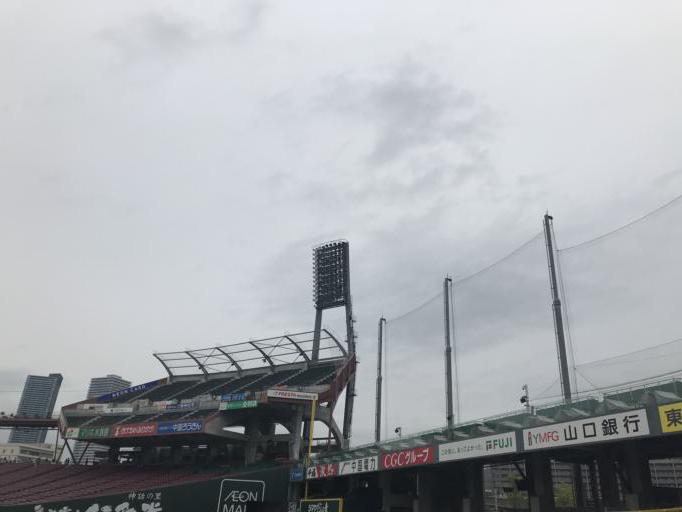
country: JP
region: Hiroshima
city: Hiroshima-shi
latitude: 34.3921
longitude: 132.4854
